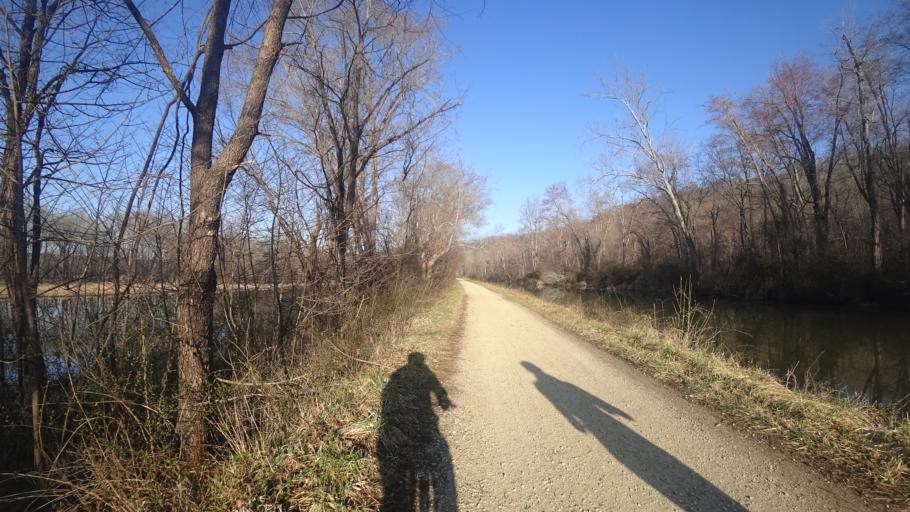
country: US
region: Maryland
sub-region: Montgomery County
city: Travilah
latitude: 39.0585
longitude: -77.3005
